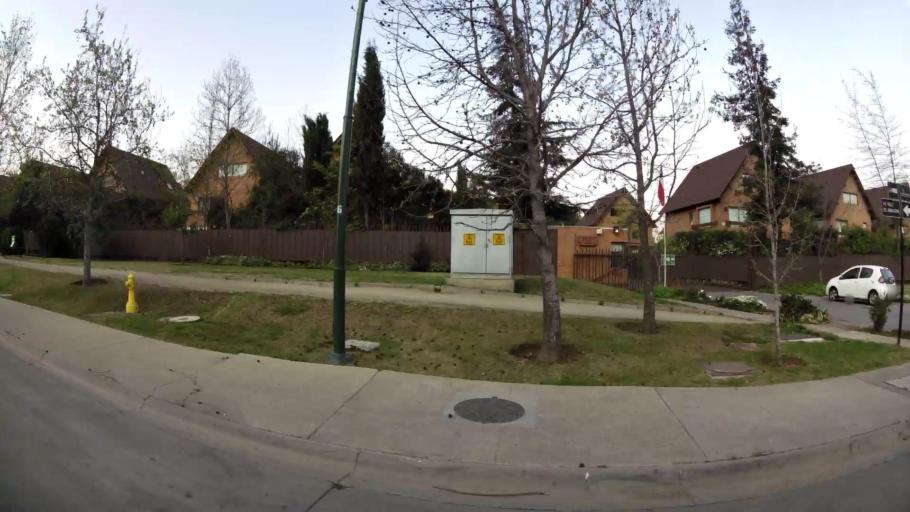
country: CL
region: Santiago Metropolitan
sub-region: Provincia de Santiago
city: Villa Presidente Frei, Nunoa, Santiago, Chile
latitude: -33.3540
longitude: -70.5455
